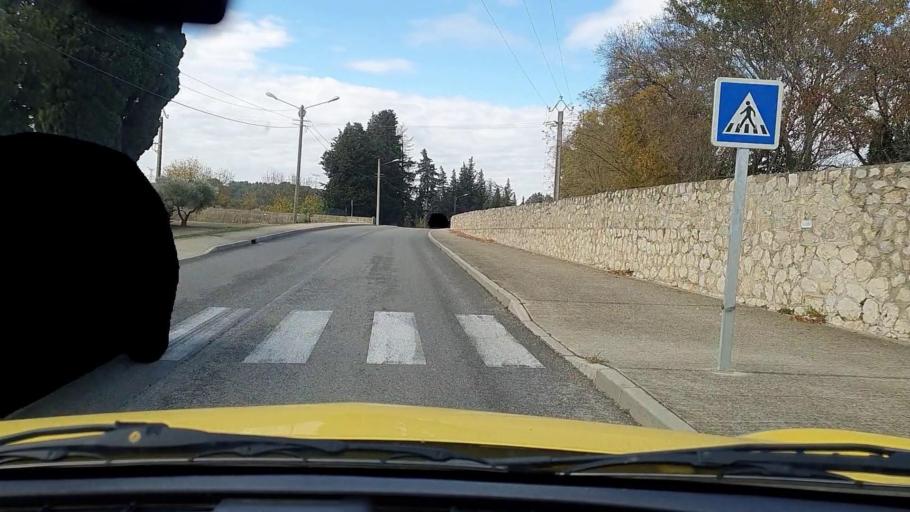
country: FR
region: Languedoc-Roussillon
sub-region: Departement du Gard
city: Comps
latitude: 43.8526
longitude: 4.6004
